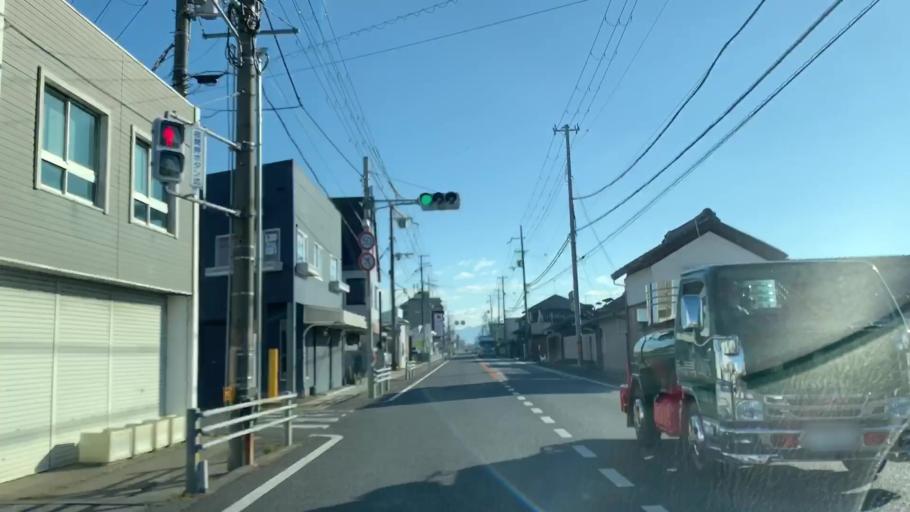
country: JP
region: Wakayama
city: Wakayama-shi
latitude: 34.2449
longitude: 135.1975
